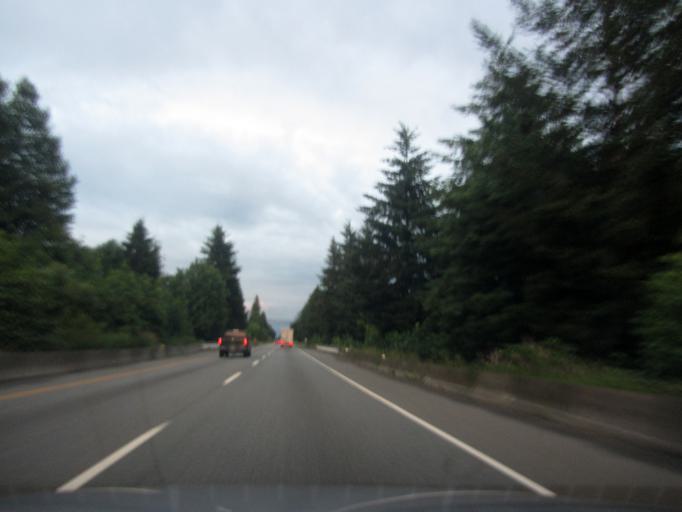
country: CA
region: British Columbia
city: Aldergrove
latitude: 49.0756
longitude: -122.4274
